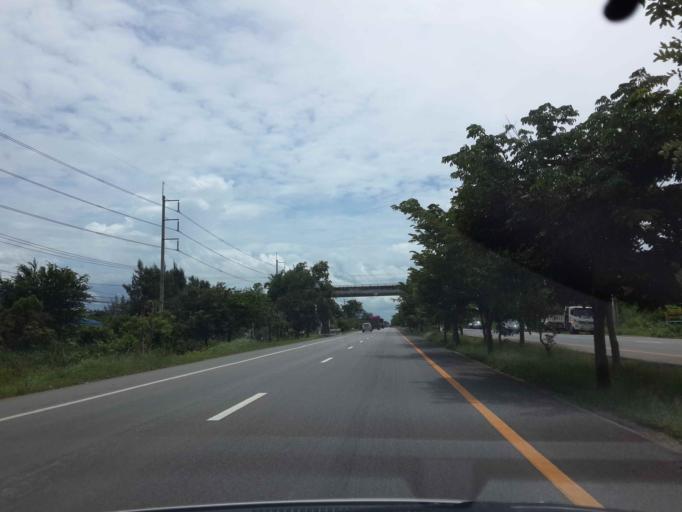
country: TH
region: Ratchaburi
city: Pak Tho
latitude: 13.4131
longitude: 99.8111
